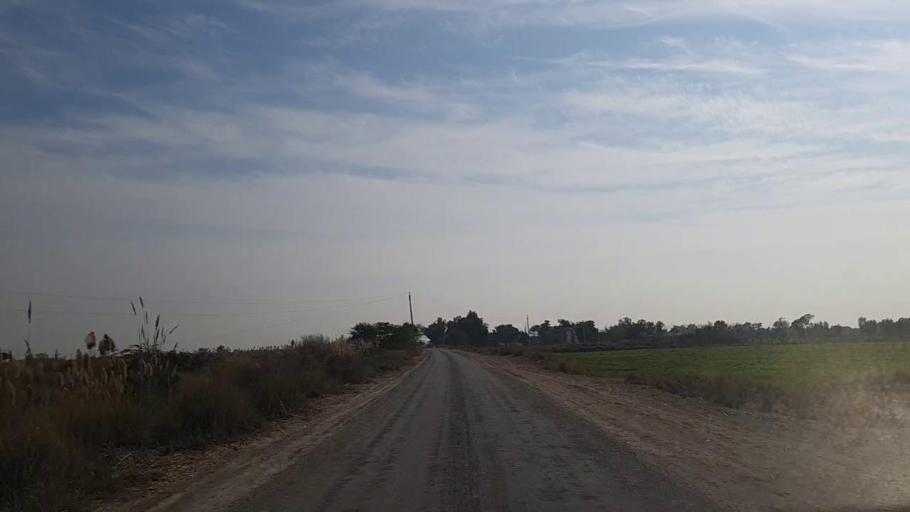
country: PK
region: Sindh
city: Daur
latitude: 26.4740
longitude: 68.4178
